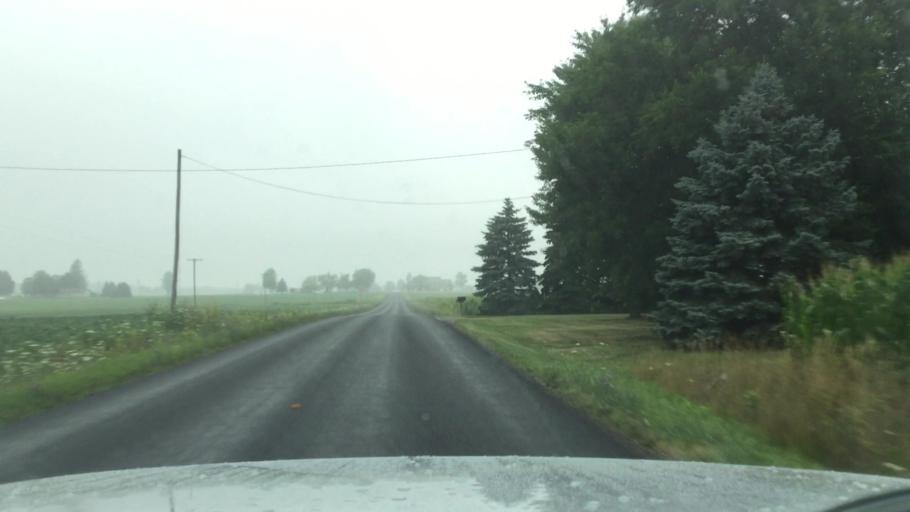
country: US
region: Michigan
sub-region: Shiawassee County
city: New Haven
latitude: 43.0574
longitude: -84.1221
